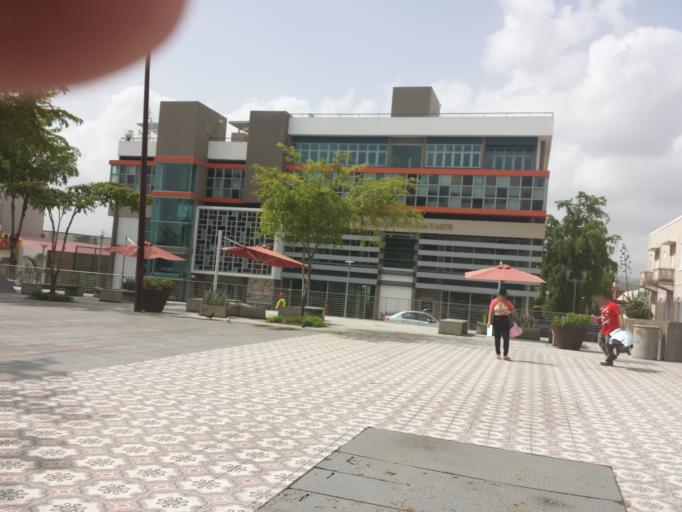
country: PR
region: Carolina
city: Carolina
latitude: 18.3810
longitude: -65.9572
